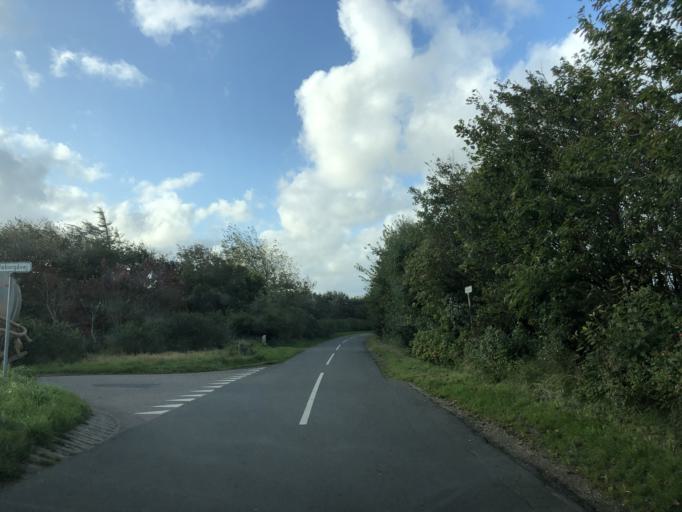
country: DK
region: Central Jutland
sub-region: Holstebro Kommune
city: Ulfborg
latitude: 56.3881
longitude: 8.3497
